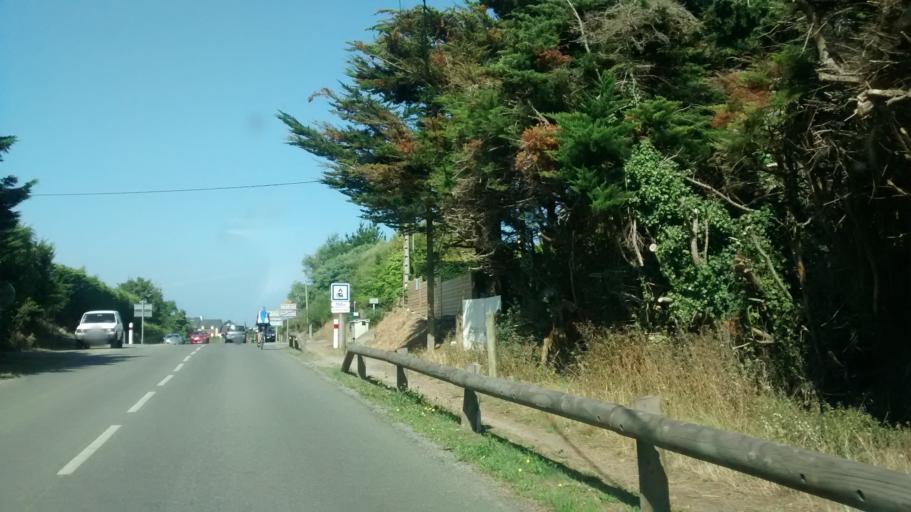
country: FR
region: Brittany
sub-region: Departement d'Ille-et-Vilaine
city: Cancale
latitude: 48.6980
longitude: -1.8526
